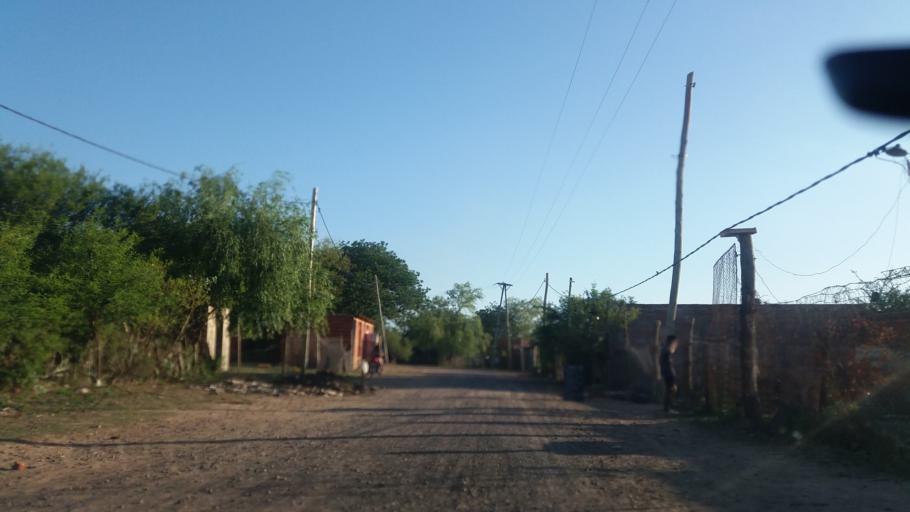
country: AR
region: Corrientes
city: Corrientes
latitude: -27.5170
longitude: -58.8297
